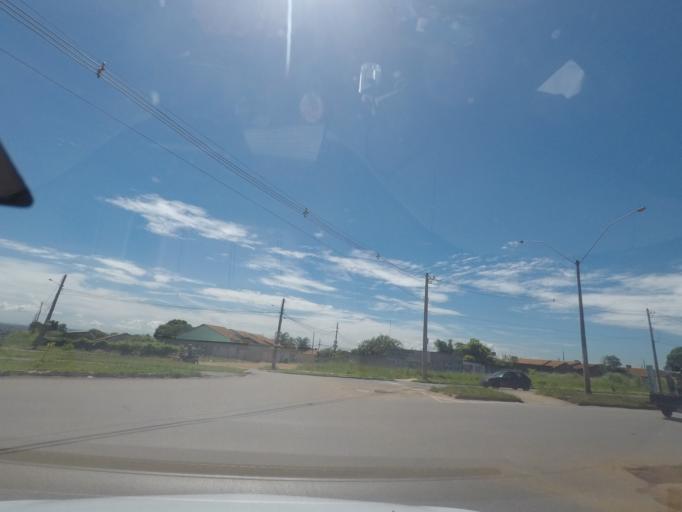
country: BR
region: Goias
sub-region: Aparecida De Goiania
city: Aparecida de Goiania
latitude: -16.7884
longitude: -49.3305
